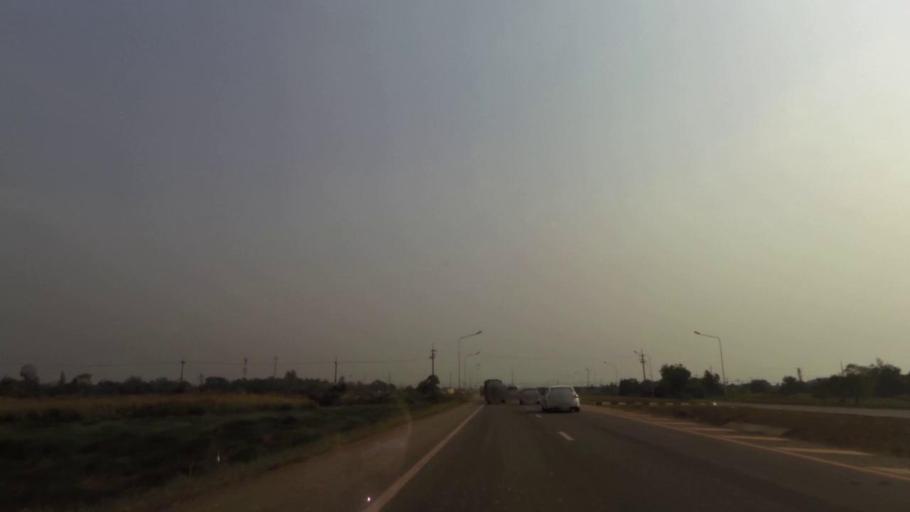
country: TH
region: Rayong
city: Klaeng
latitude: 12.7892
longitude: 101.6756
